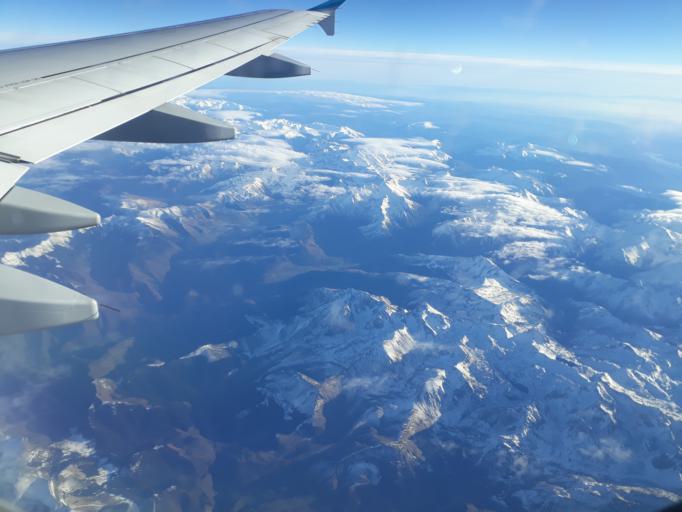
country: FR
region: Midi-Pyrenees
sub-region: Departement des Hautes-Pyrenees
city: Campan
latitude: 43.0196
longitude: 0.1724
